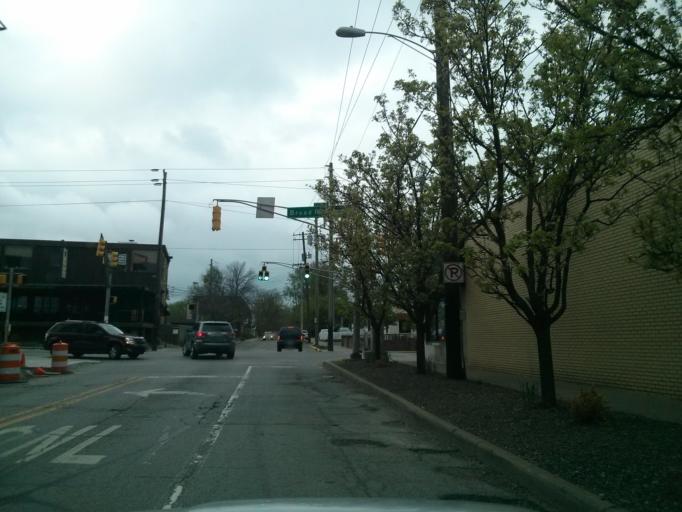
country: US
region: Indiana
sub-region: Marion County
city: Broad Ripple
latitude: 39.8701
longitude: -86.1418
